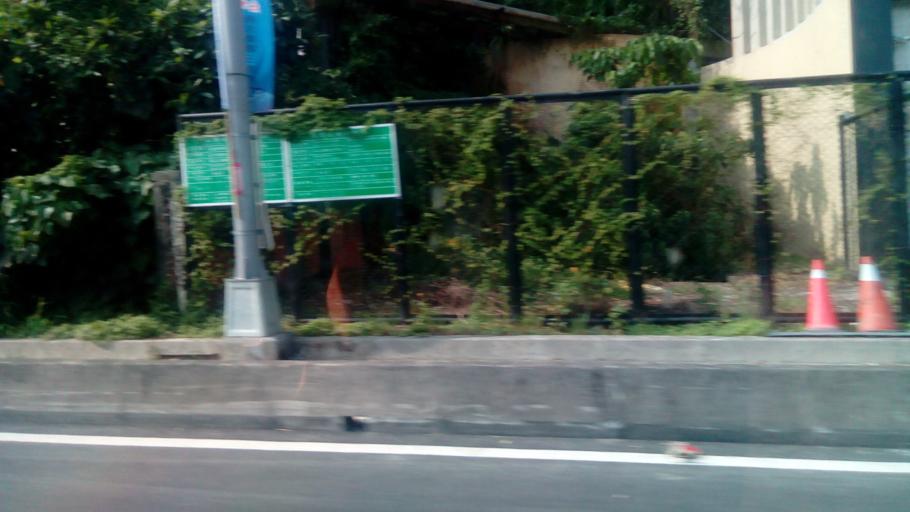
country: TW
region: Taiwan
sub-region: Yilan
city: Yilan
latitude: 24.5885
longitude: 121.8618
